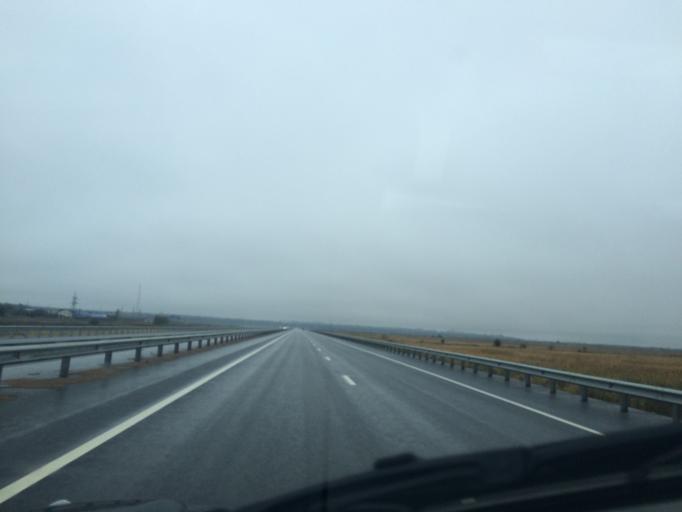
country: RU
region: Rostov
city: Kuleshovka
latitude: 47.0893
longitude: 39.5171
